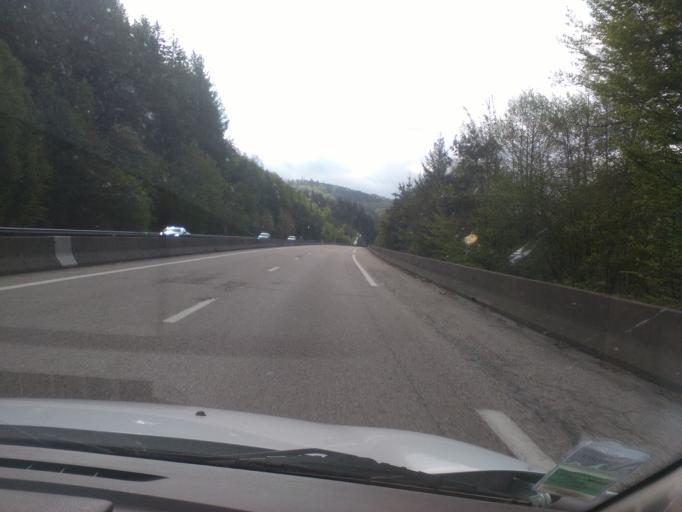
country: FR
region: Lorraine
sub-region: Departement des Vosges
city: Arches
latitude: 48.1473
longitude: 6.5033
